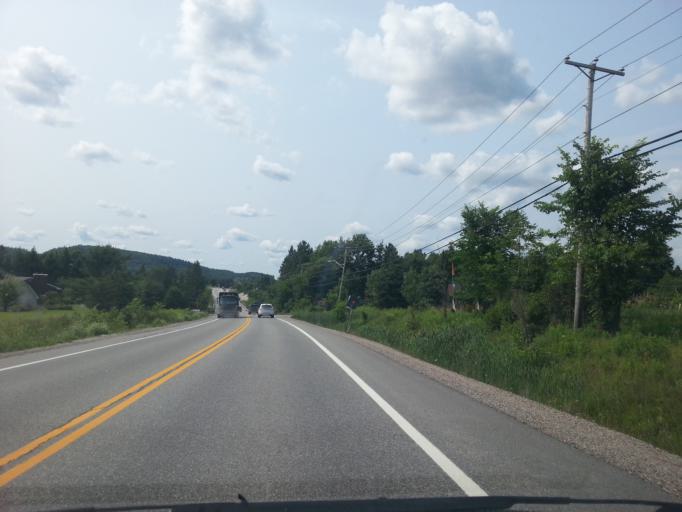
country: CA
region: Quebec
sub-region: Outaouais
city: Wakefield
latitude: 45.5948
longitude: -75.8939
